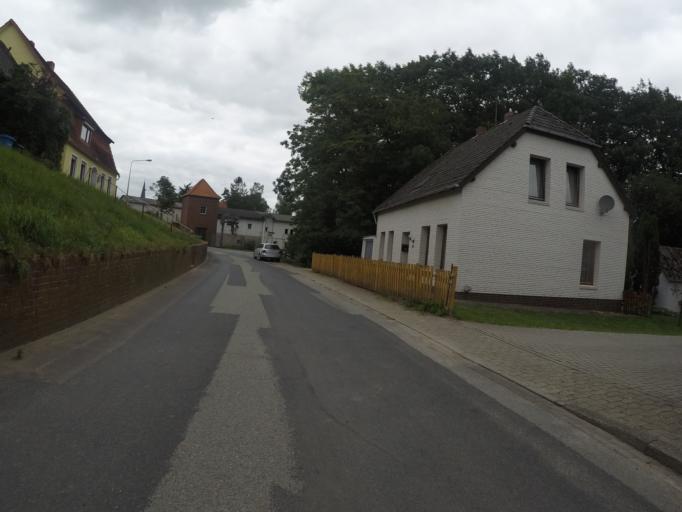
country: DE
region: Lower Saxony
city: Osten
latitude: 53.6934
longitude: 9.1916
